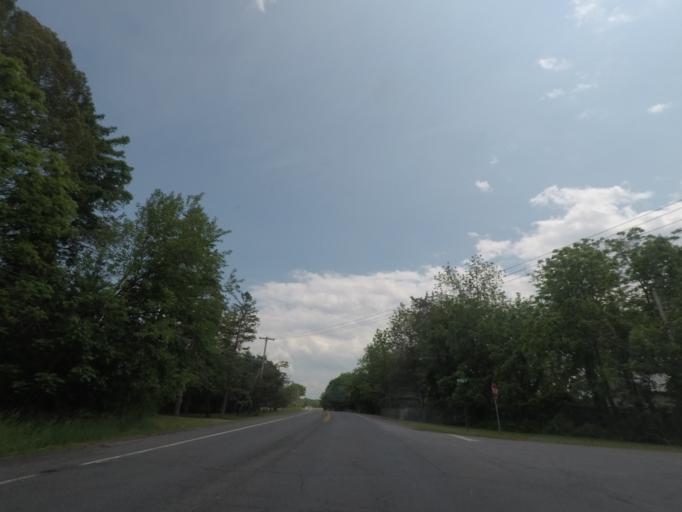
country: US
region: New York
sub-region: Columbia County
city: Oakdale
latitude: 42.1720
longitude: -73.7576
